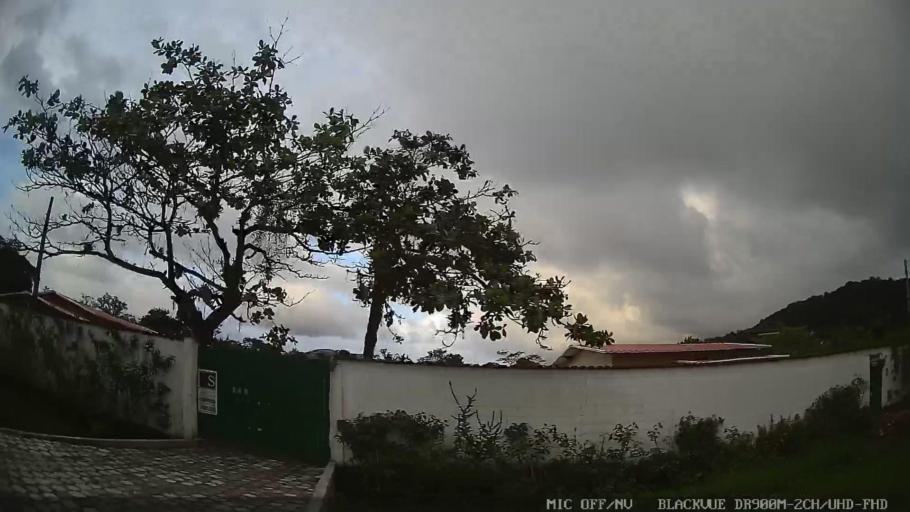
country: BR
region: Sao Paulo
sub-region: Itanhaem
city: Itanhaem
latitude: -24.1214
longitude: -46.7842
